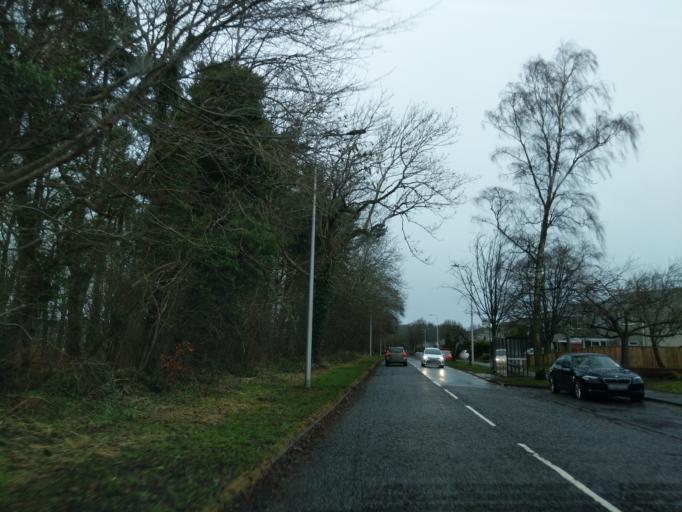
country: GB
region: Scotland
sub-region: Edinburgh
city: Balerno
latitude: 55.8751
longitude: -3.3466
